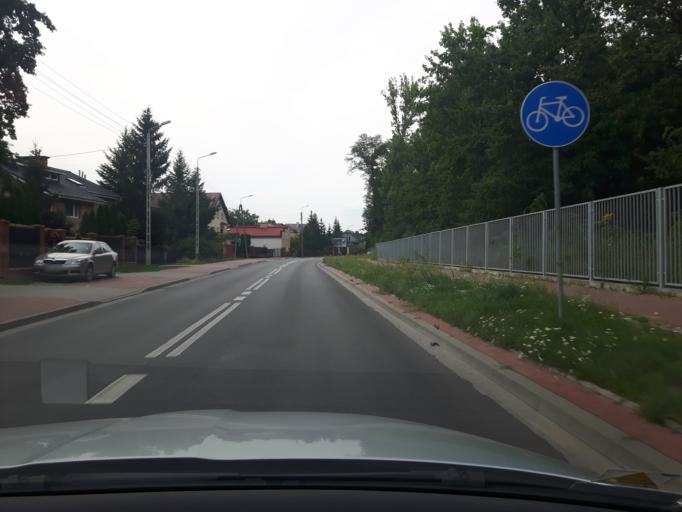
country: PL
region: Masovian Voivodeship
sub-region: Powiat wolominski
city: Zabki
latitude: 52.3021
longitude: 21.1071
